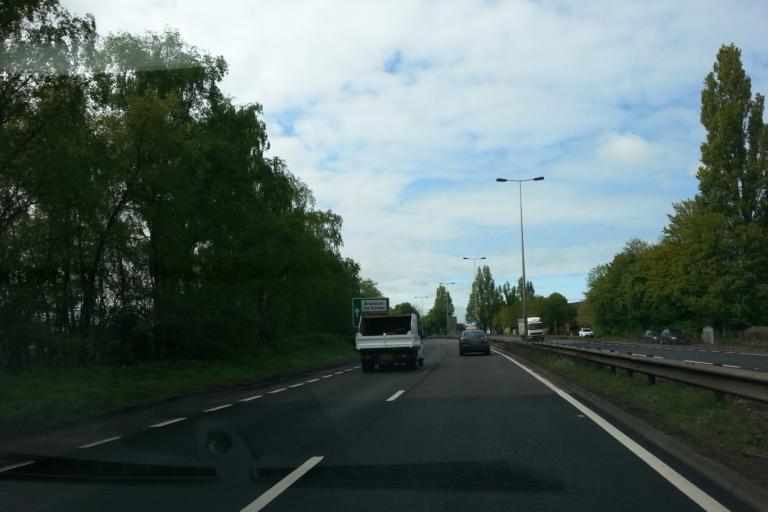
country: GB
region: England
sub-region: Staffordshire
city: Burton upon Trent
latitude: 52.7823
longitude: -1.6803
